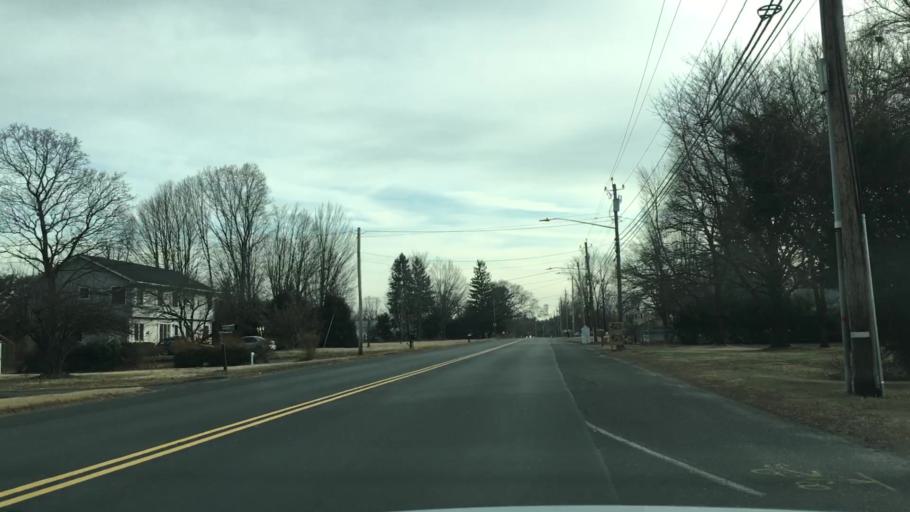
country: US
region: Massachusetts
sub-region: Hampden County
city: Westfield
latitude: 42.0965
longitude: -72.7631
